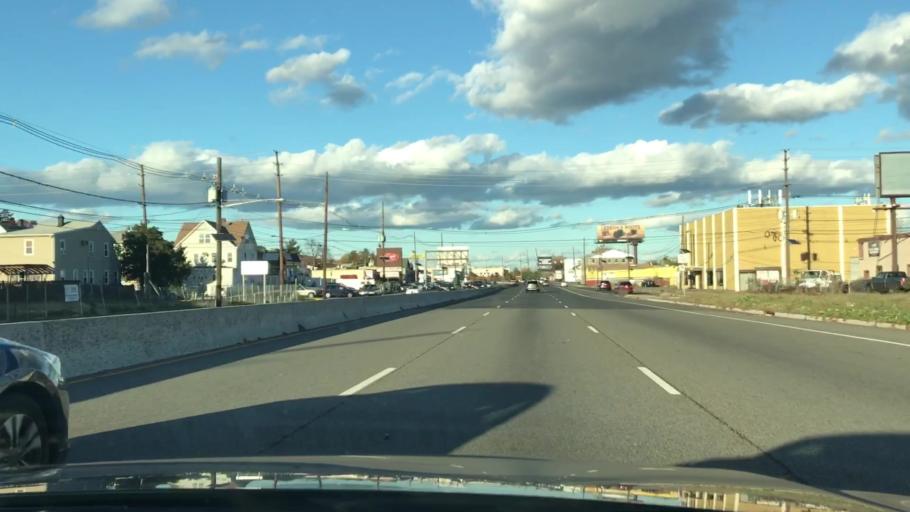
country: US
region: New Jersey
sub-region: Bergen County
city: Carlstadt
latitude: 40.8339
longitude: -74.0875
